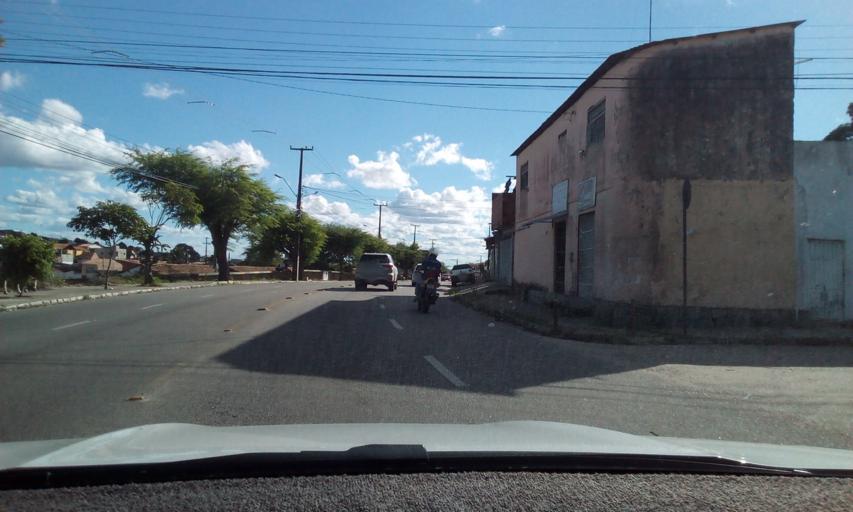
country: BR
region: Paraiba
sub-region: Campina Grande
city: Campina Grande
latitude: -7.2293
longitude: -35.8982
